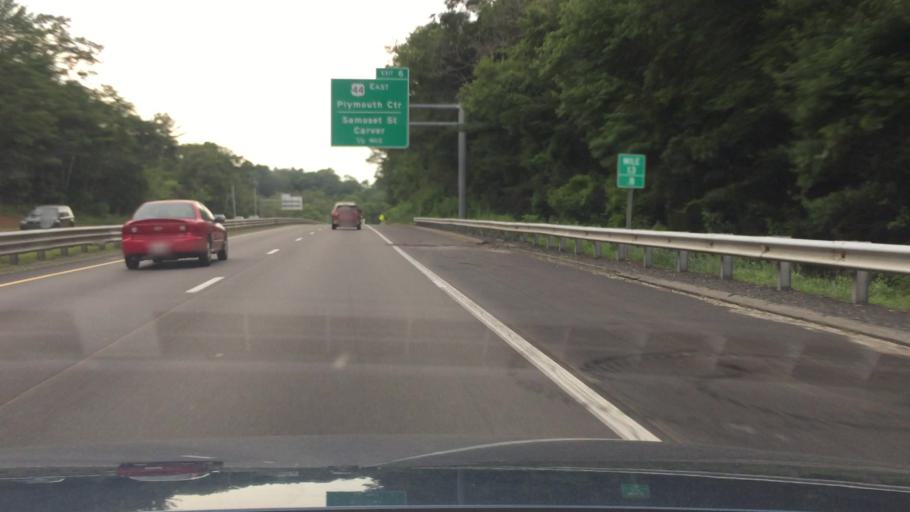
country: US
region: Massachusetts
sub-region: Plymouth County
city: Plymouth
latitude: 41.9426
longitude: -70.6725
